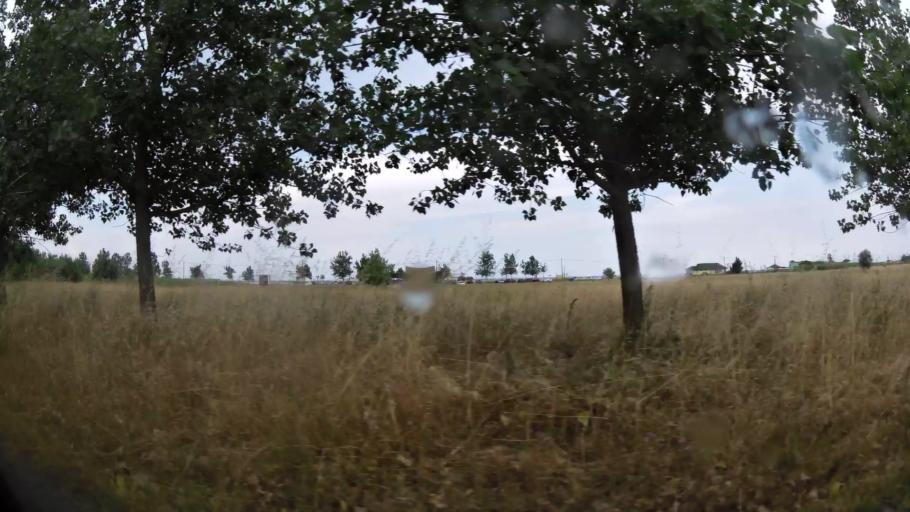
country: GR
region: Central Macedonia
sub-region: Nomos Pierias
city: Paralia
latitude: 40.2807
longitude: 22.6011
